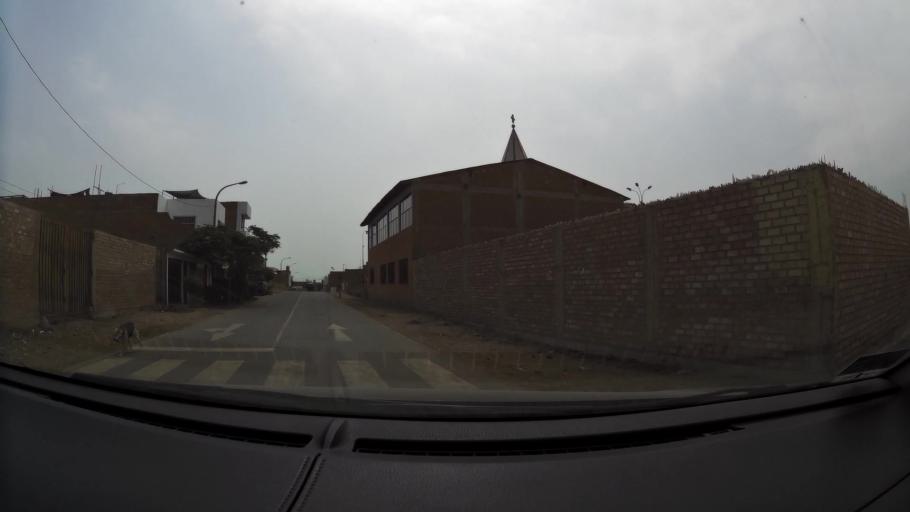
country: PE
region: Lima
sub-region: Lima
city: Santa Rosa
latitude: -11.7878
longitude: -77.1552
